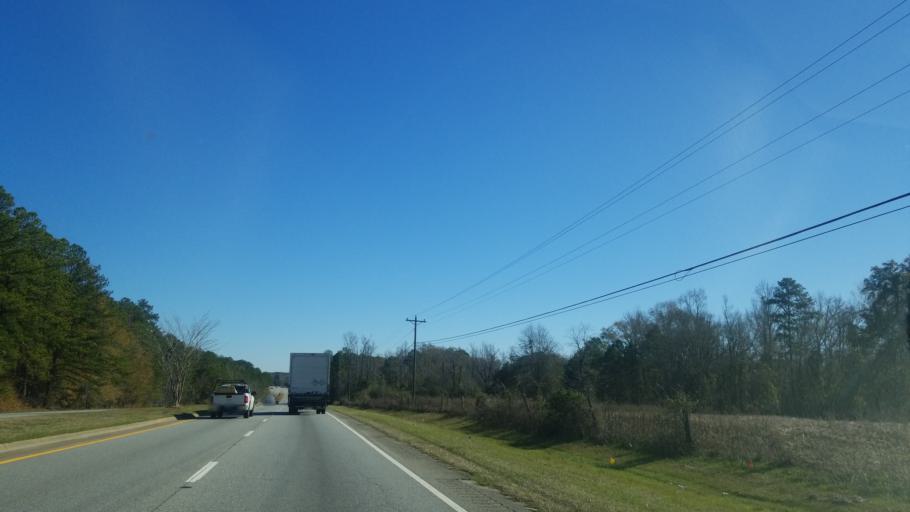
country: US
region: Georgia
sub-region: Muscogee County
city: Columbus
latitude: 32.5380
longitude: -84.8542
